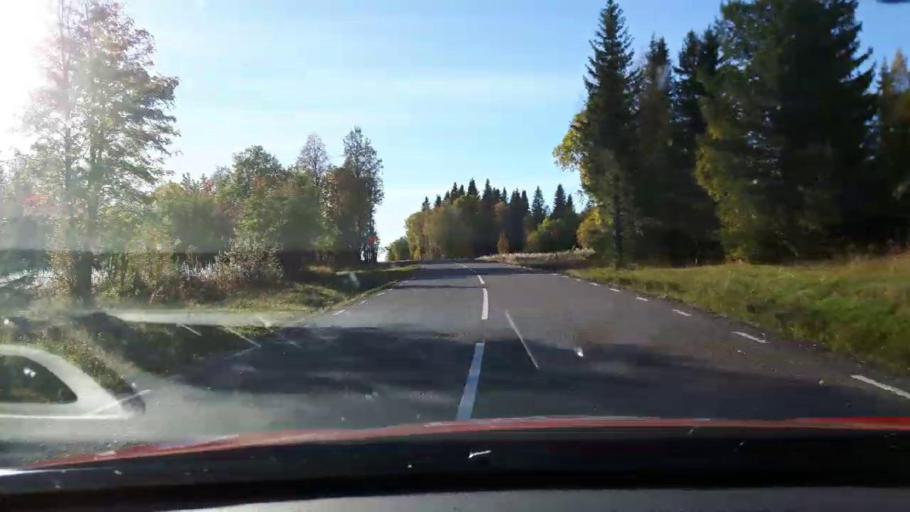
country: SE
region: Jaemtland
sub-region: Stroemsunds Kommun
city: Stroemsund
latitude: 63.8655
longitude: 15.1399
